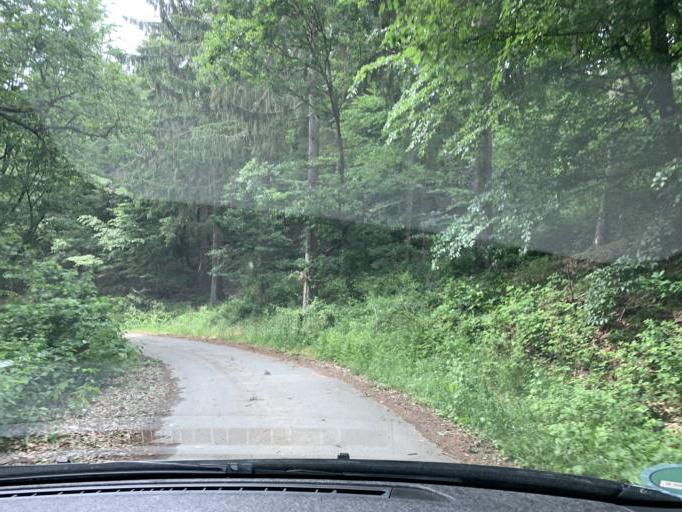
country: DE
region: North Rhine-Westphalia
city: Heimbach
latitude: 50.6488
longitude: 6.4126
